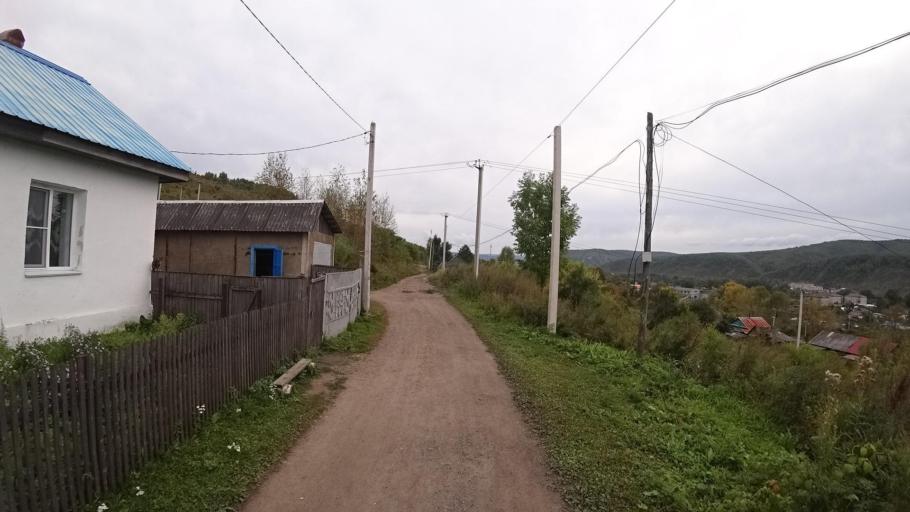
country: RU
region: Jewish Autonomous Oblast
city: Khingansk
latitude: 49.0341
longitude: 131.0604
